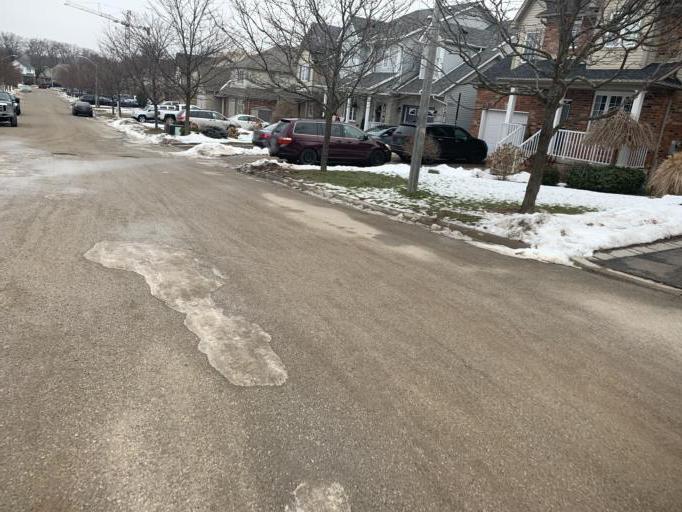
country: CA
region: Ontario
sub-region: Halton
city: Milton
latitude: 43.6587
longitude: -79.9203
